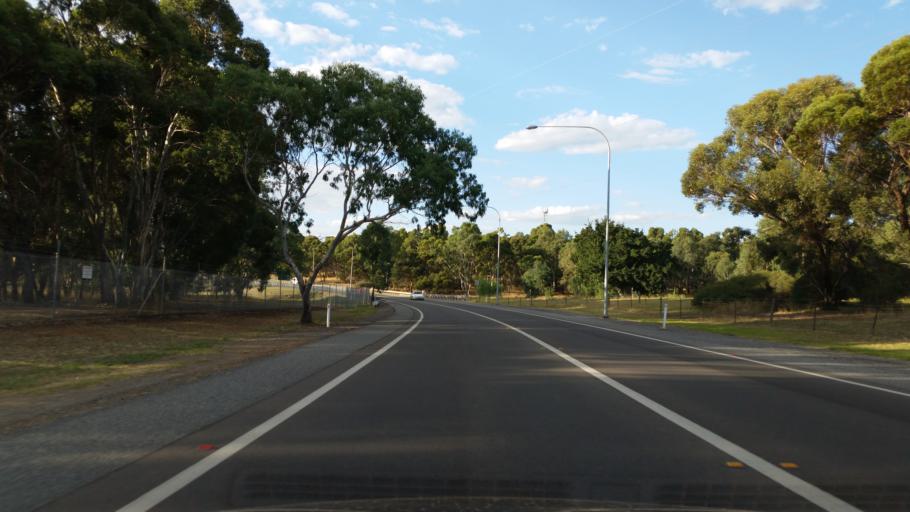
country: AU
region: South Australia
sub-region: Marion
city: Trott Park
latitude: -35.0773
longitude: 138.5826
